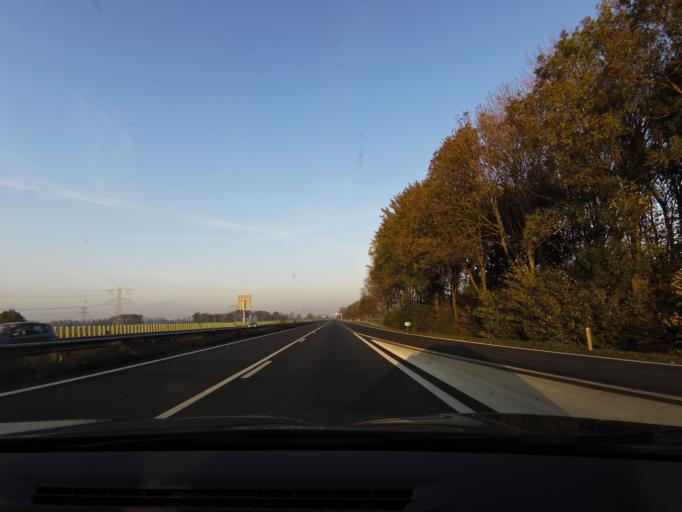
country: NL
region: North Brabant
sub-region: Gemeente Moerdijk
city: Klundert
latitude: 51.6438
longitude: 4.5578
